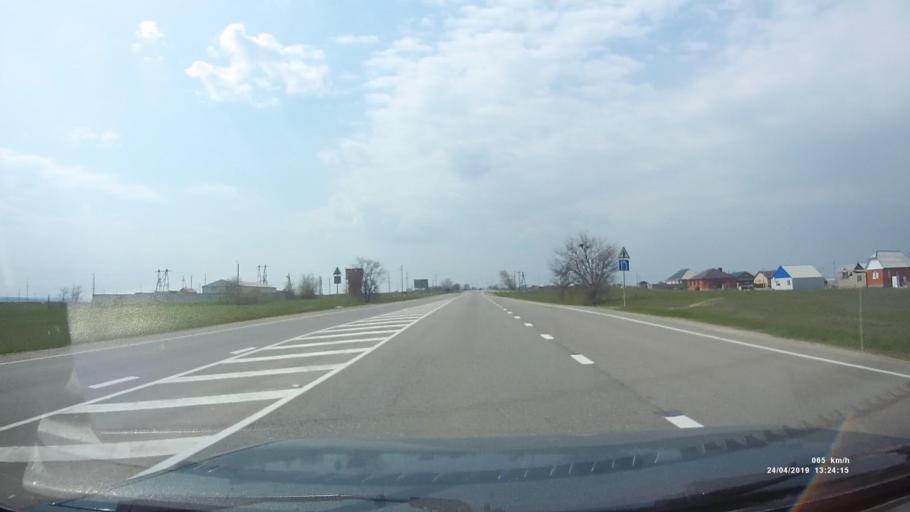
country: RU
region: Kalmykiya
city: Elista
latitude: 46.2842
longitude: 44.2584
